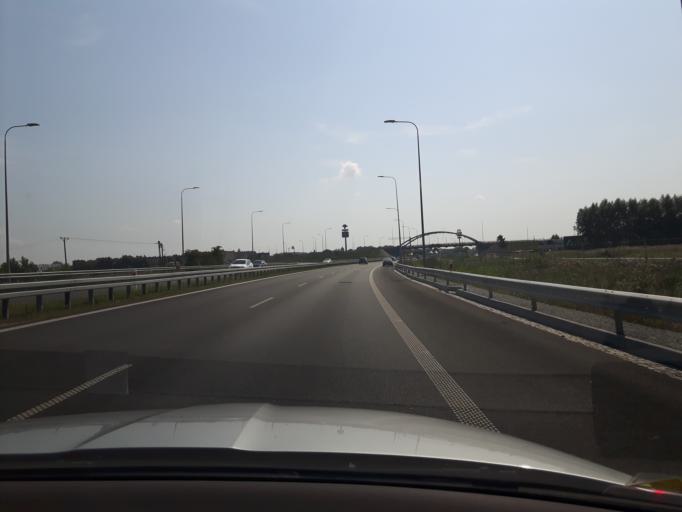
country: PL
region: Pomeranian Voivodeship
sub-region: Powiat nowodworski
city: Nowy Dwor Gdanski
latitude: 54.2149
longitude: 19.0987
